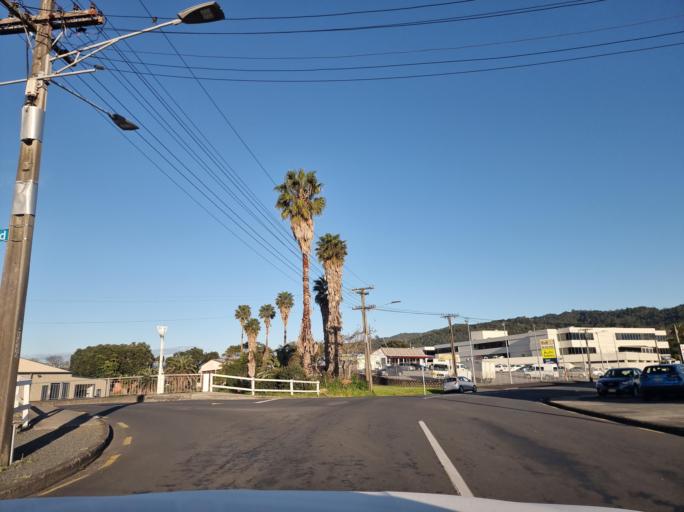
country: NZ
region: Northland
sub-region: Whangarei
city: Whangarei
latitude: -35.7284
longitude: 174.3222
